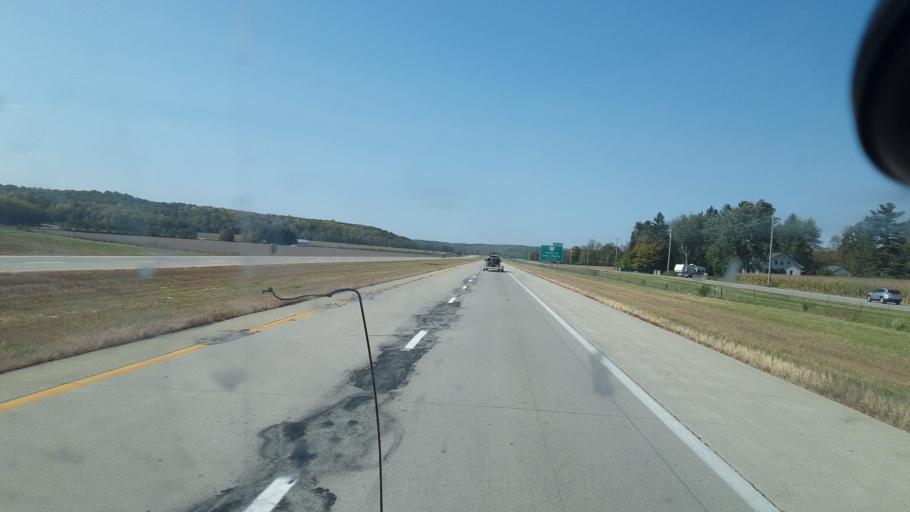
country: US
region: Ohio
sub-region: Logan County
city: Bellefontaine
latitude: 40.3264
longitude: -83.6387
